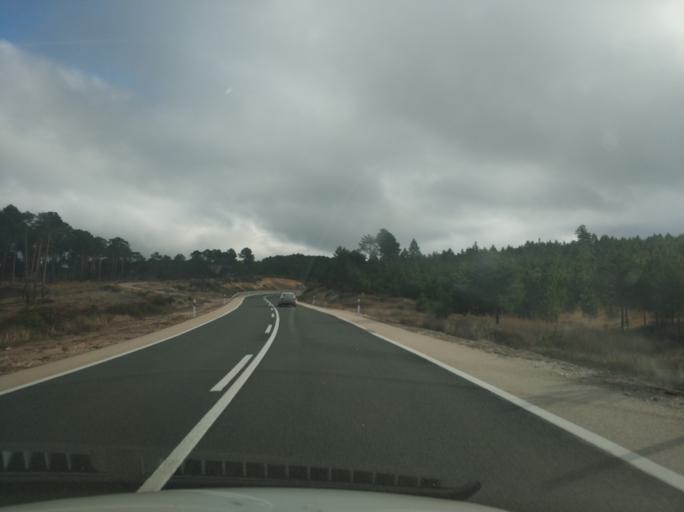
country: ES
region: Castille and Leon
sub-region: Provincia de Soria
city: Navaleno
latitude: 41.8278
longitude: -2.9569
